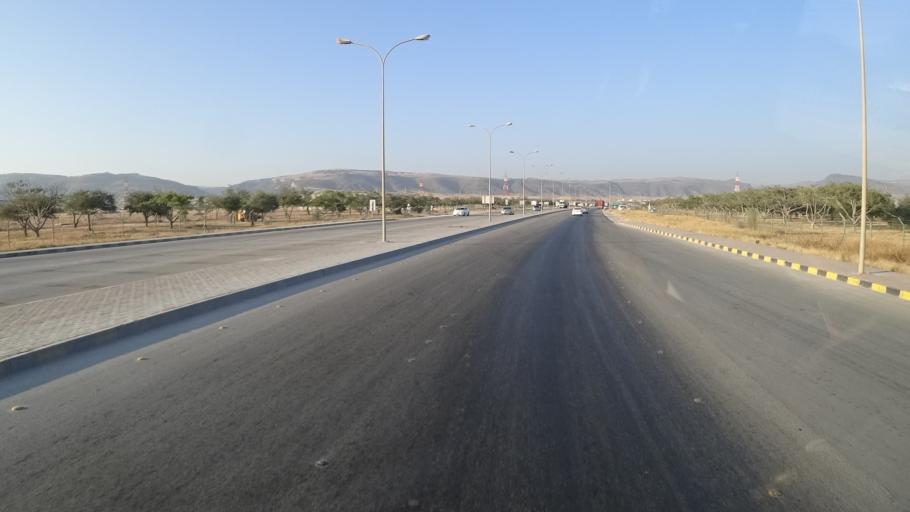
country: OM
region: Zufar
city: Salalah
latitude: 17.0976
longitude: 54.1486
